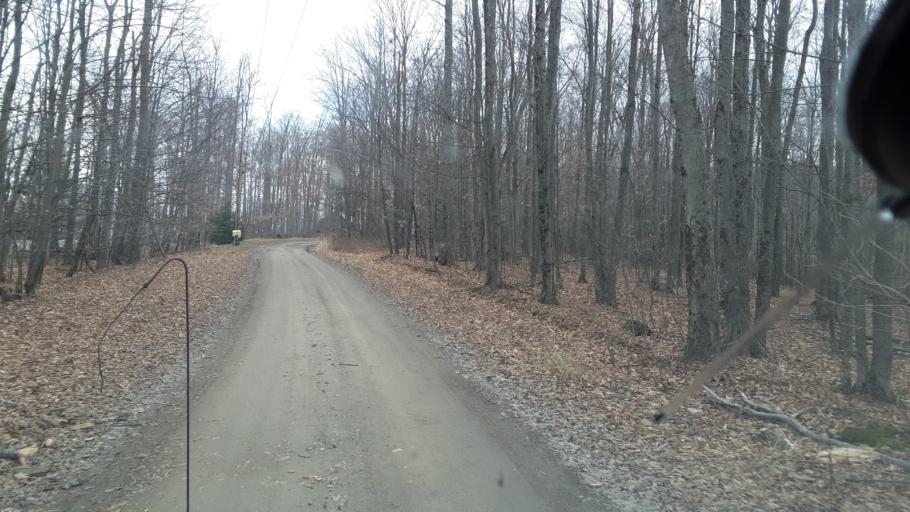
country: US
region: Pennsylvania
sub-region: Tioga County
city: Westfield
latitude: 41.9211
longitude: -77.7039
